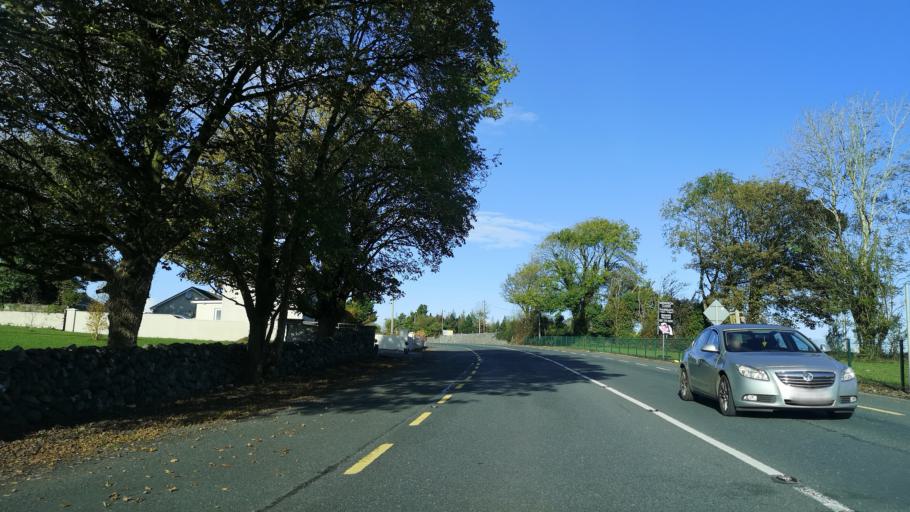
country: IE
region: Connaught
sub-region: County Galway
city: Moycullen
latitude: 53.4461
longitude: -9.0851
